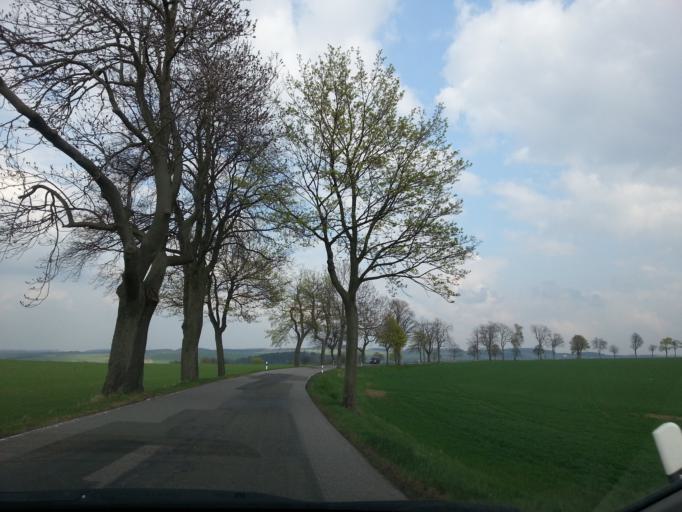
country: DE
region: Saxony
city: Frauenstein
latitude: 50.7949
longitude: 13.5512
